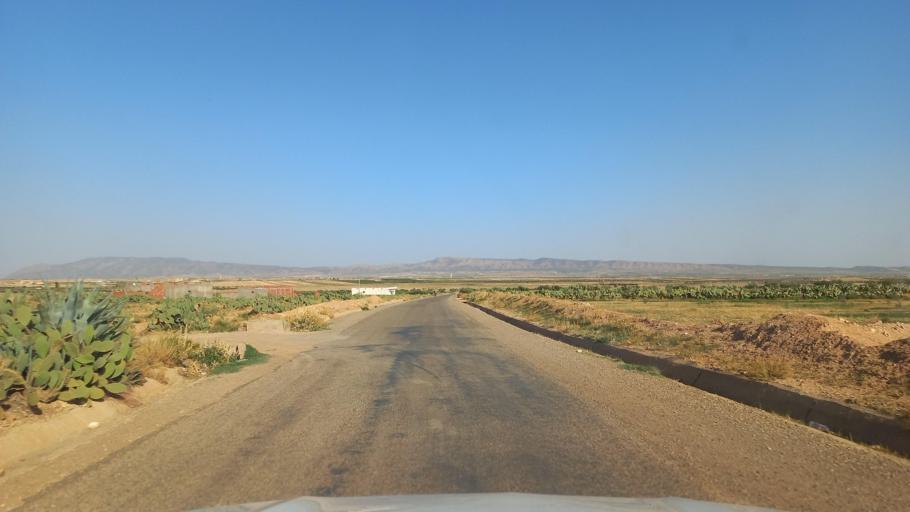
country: TN
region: Al Qasrayn
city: Sbiba
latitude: 35.3789
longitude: 9.0246
